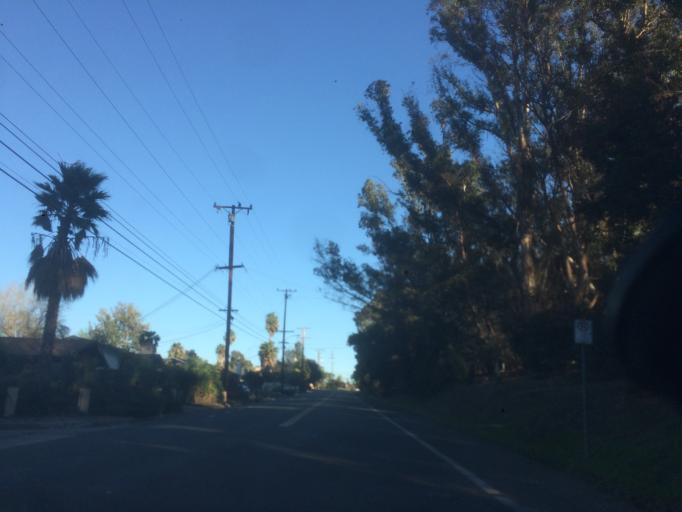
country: US
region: California
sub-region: Santa Barbara County
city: Mission Canyon
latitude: 34.4369
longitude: -119.7570
